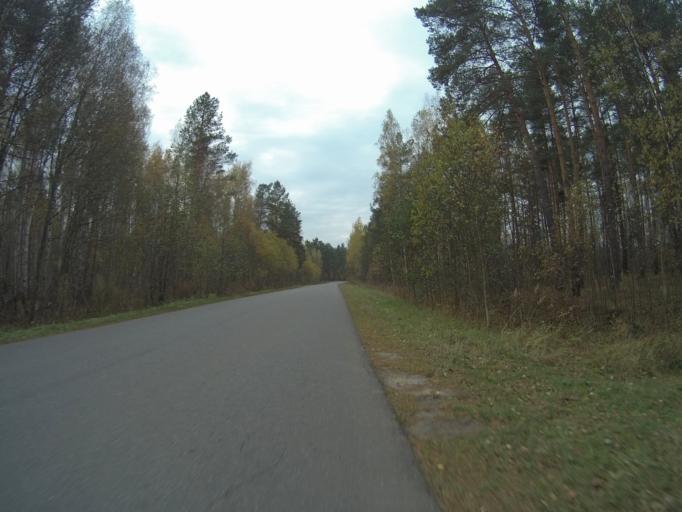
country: RU
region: Vladimir
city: Bogolyubovo
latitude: 56.1494
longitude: 40.5283
